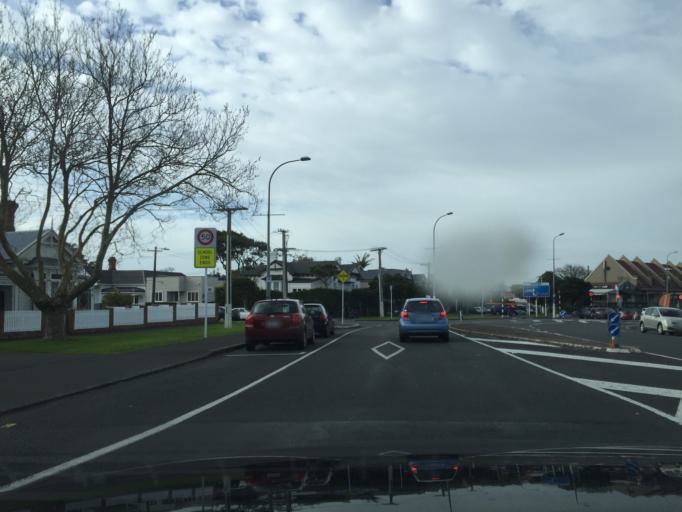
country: NZ
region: Auckland
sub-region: Auckland
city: Auckland
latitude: -36.8632
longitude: 174.7367
